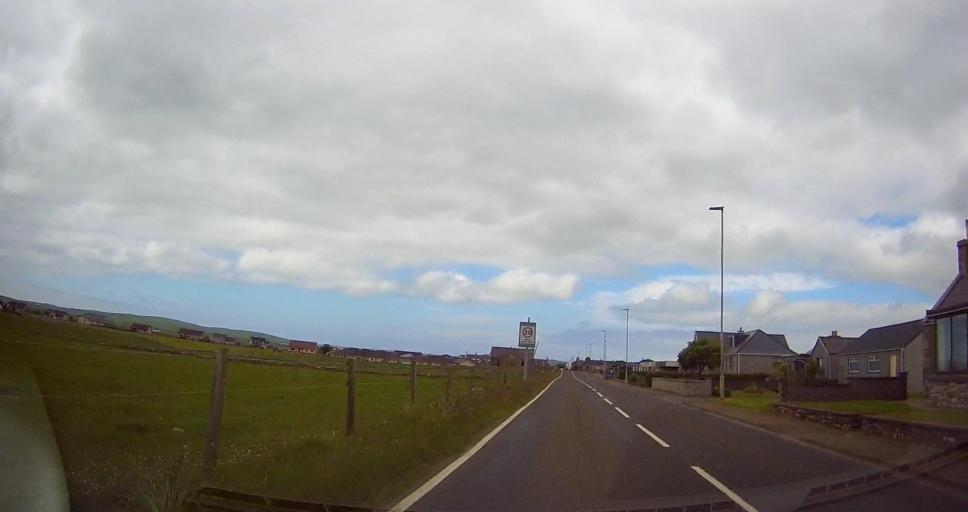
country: GB
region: Scotland
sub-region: Orkney Islands
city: Stromness
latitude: 59.0653
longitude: -3.2270
